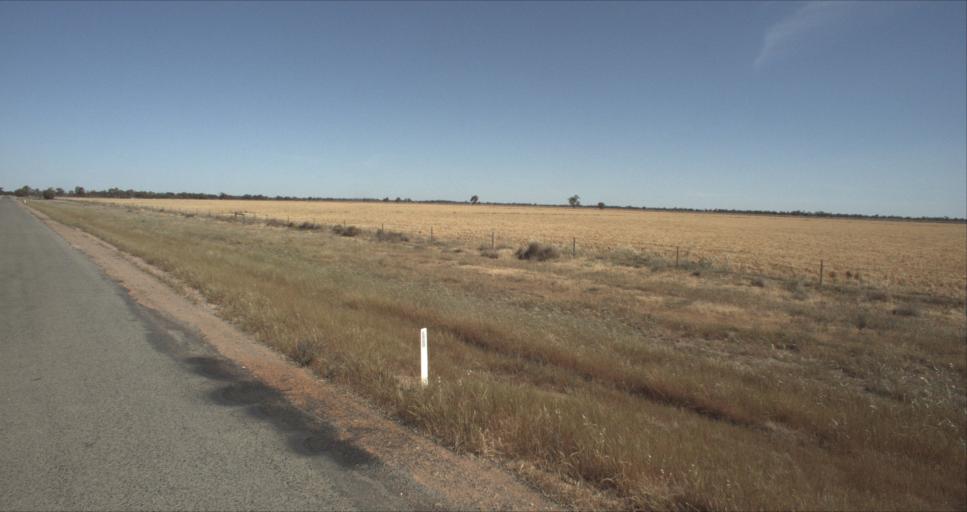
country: AU
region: New South Wales
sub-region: Leeton
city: Leeton
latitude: -34.4923
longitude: 146.3848
